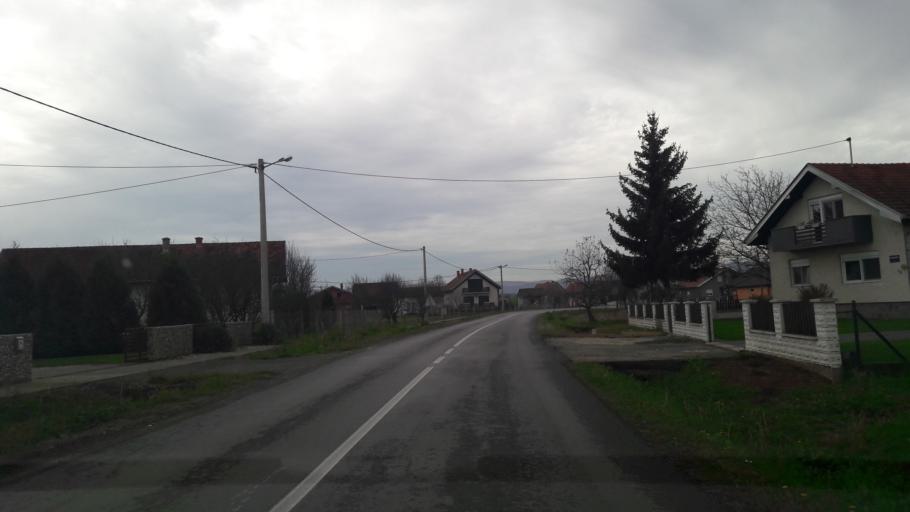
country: HR
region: Osjecko-Baranjska
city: Martin
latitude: 45.5309
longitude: 18.0311
